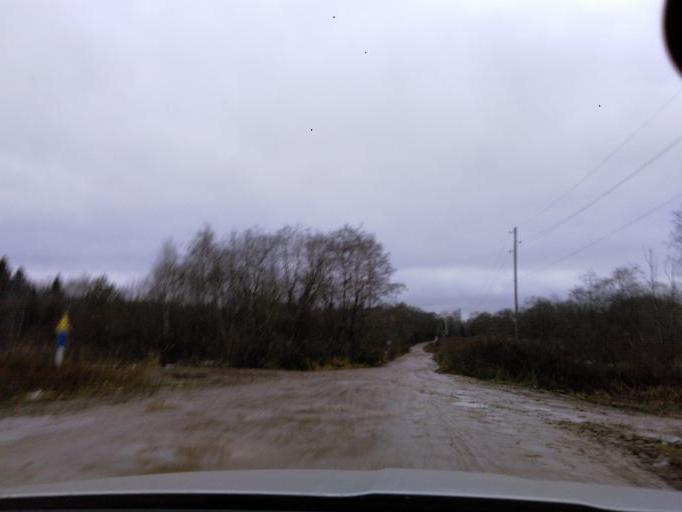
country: RU
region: Moskovskaya
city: Lozhki
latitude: 56.0580
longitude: 37.1124
